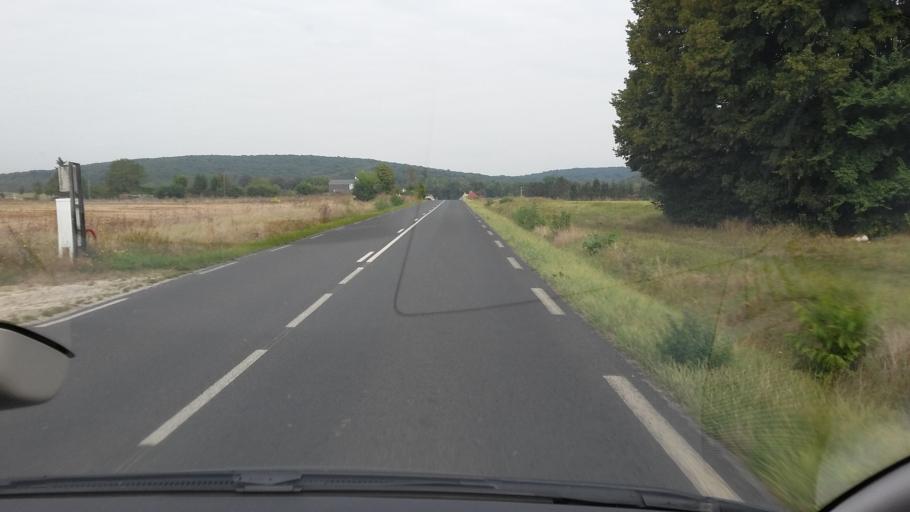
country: FR
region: Champagne-Ardenne
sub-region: Departement de la Marne
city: Tours-sur-Marne
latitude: 49.0976
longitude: 4.1094
